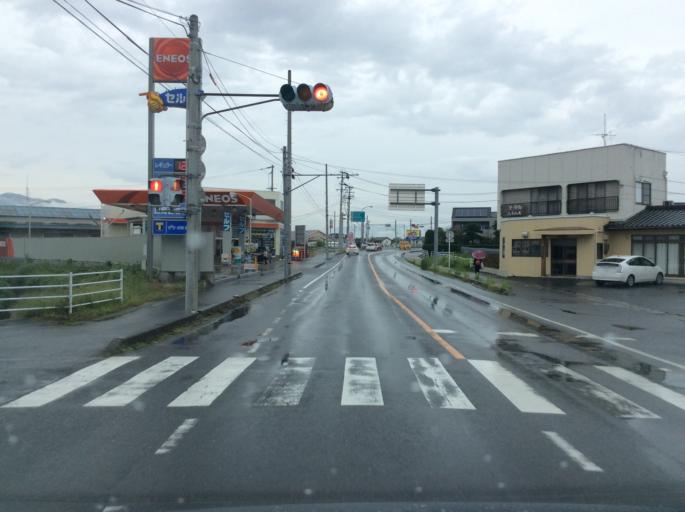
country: JP
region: Fukushima
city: Iwaki
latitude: 37.0687
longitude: 140.8815
